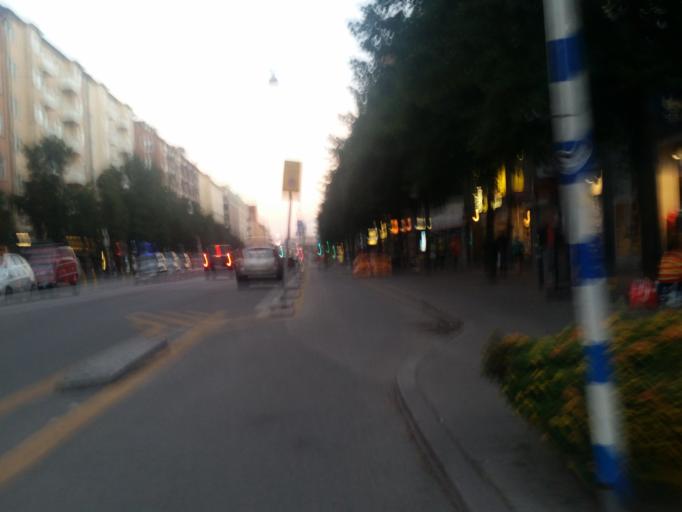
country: SE
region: Stockholm
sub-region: Stockholms Kommun
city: Stockholm
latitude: 59.3104
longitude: 18.0751
